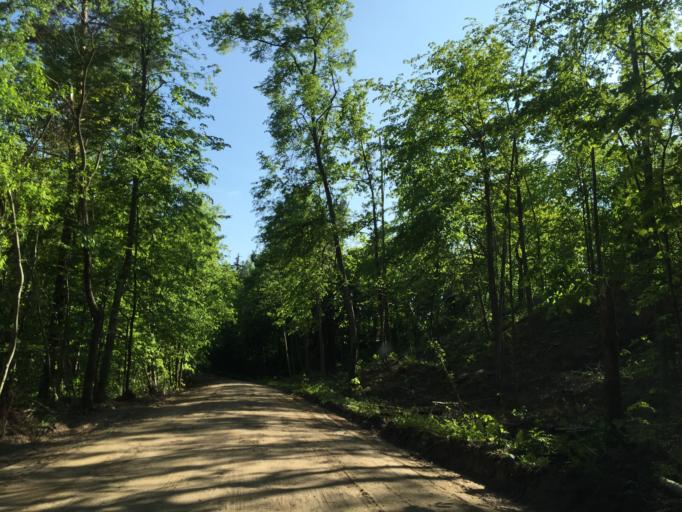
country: LV
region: Ikskile
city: Ikskile
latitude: 56.8279
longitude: 24.4311
